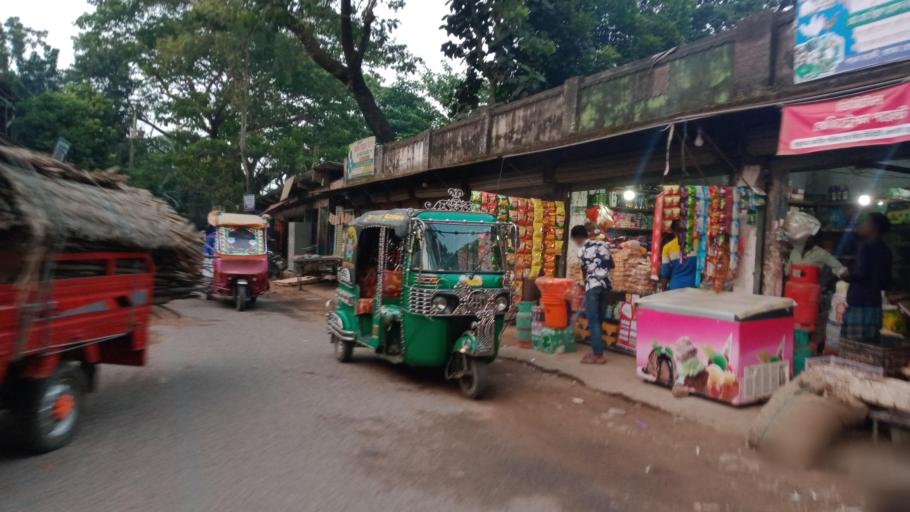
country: BD
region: Chittagong
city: Hajiganj
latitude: 23.3783
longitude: 90.9847
